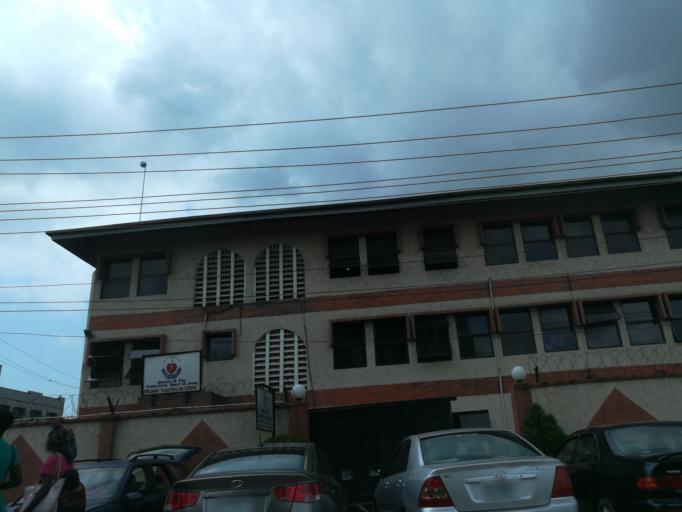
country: NG
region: Lagos
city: Ikeja
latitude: 6.5973
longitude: 3.3499
